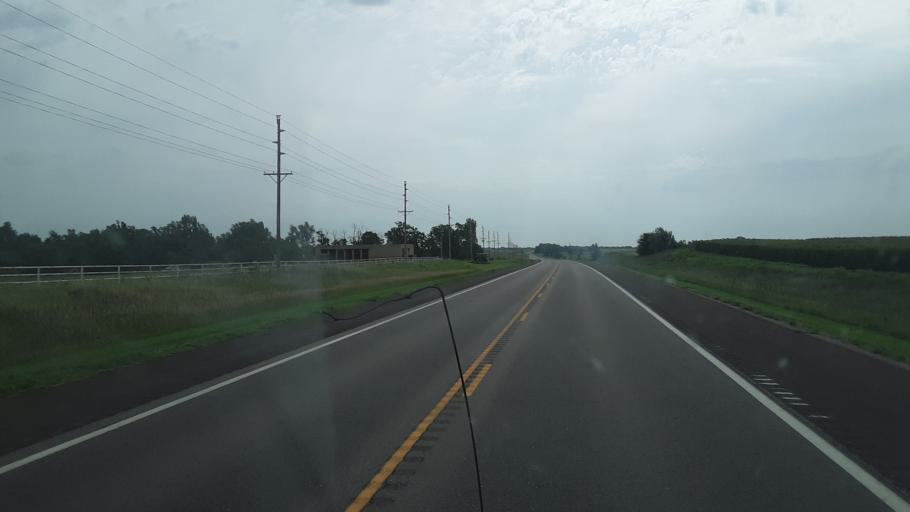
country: US
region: Kansas
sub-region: Stafford County
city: Stafford
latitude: 37.9549
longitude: -98.4958
